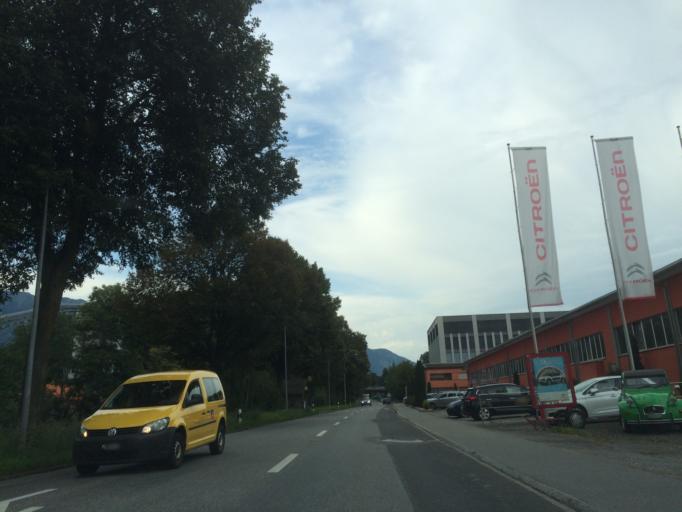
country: CH
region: Saint Gallen
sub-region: Wahlkreis Werdenberg
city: Haag (Rheintal)
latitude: 47.2069
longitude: 9.5021
